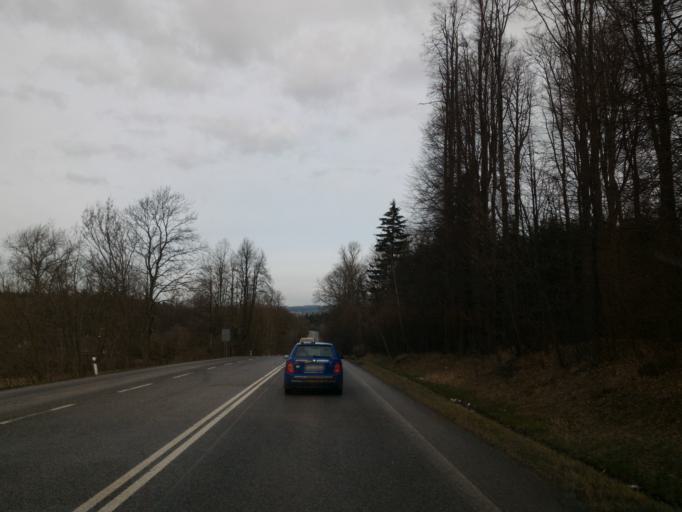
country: CZ
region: Ustecky
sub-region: Okres Decin
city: Rumburk
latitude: 50.9163
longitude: 14.5651
